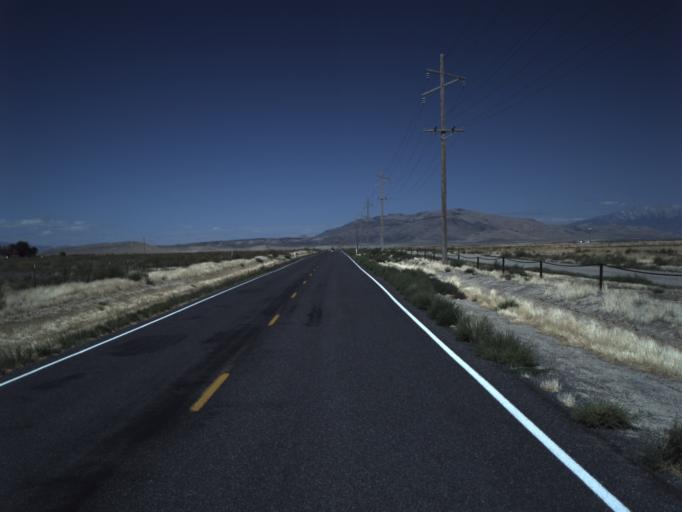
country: US
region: Utah
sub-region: Utah County
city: Genola
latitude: 40.0500
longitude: -111.9582
